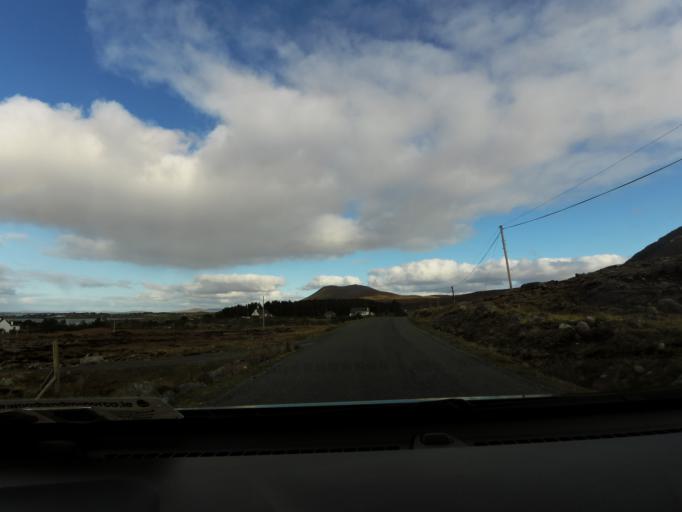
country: IE
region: Connaught
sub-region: Maigh Eo
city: Belmullet
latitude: 53.9093
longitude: -9.9201
